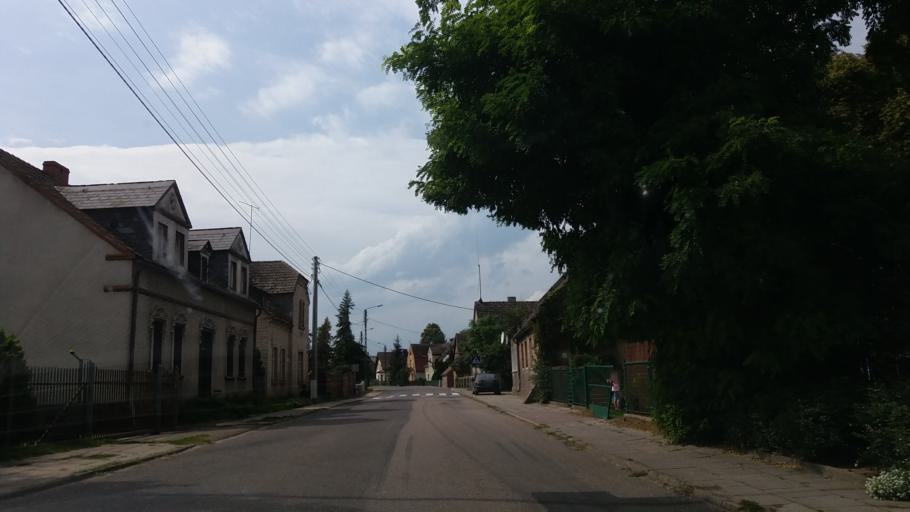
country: PL
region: Lubusz
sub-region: Powiat strzelecko-drezdenecki
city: Zwierzyn
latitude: 52.7238
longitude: 15.5354
